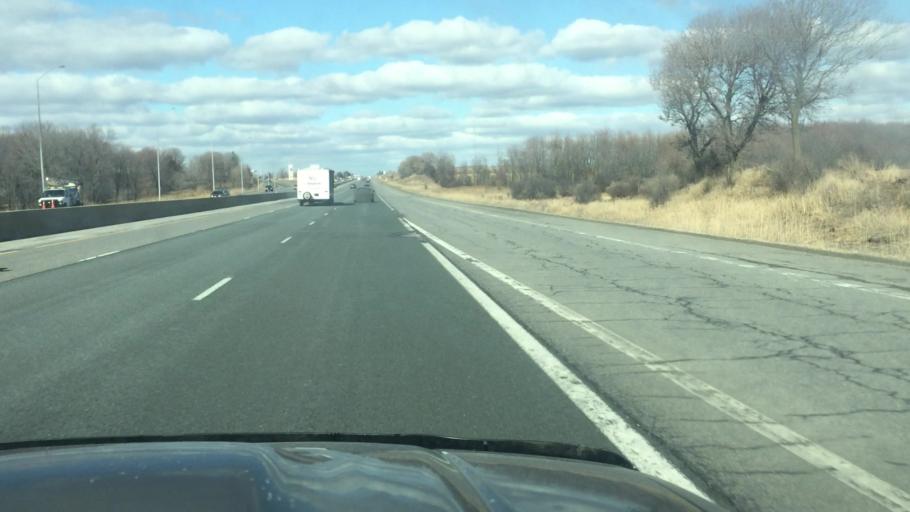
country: CA
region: Ontario
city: Ingersoll
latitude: 43.0528
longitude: -80.8185
